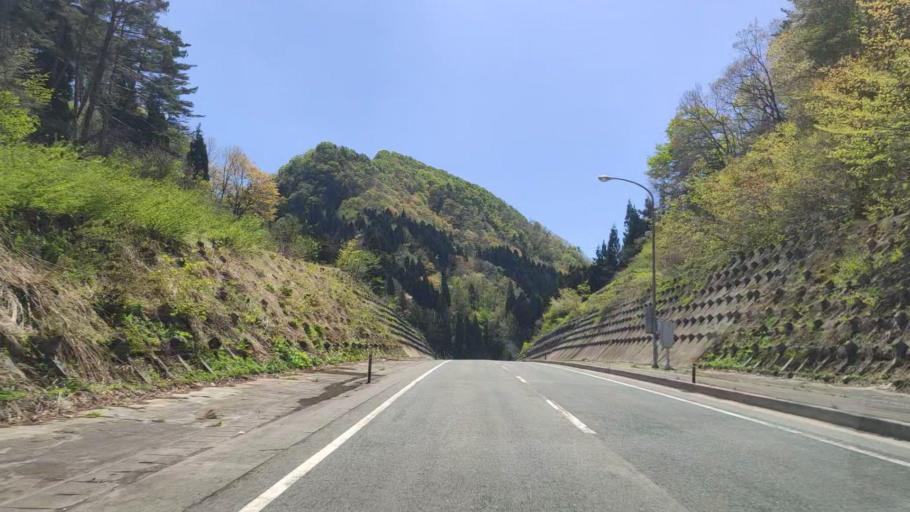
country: JP
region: Yamagata
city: Shinjo
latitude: 38.9003
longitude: 140.3276
